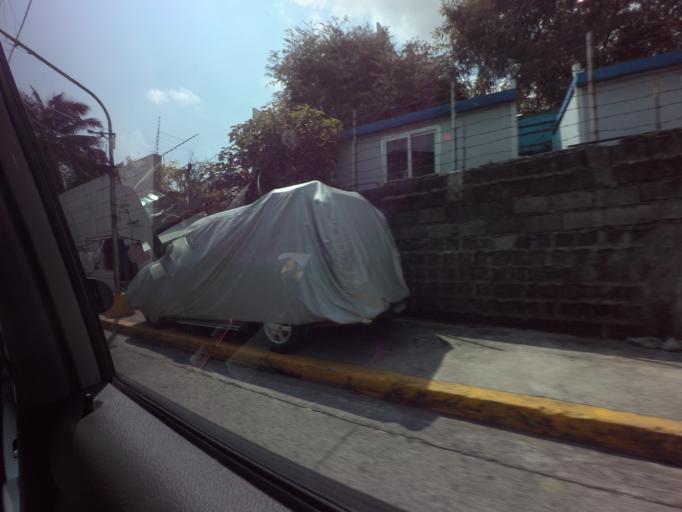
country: PH
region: Metro Manila
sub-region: City of Manila
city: Quiapo
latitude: 14.6013
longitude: 121.0073
